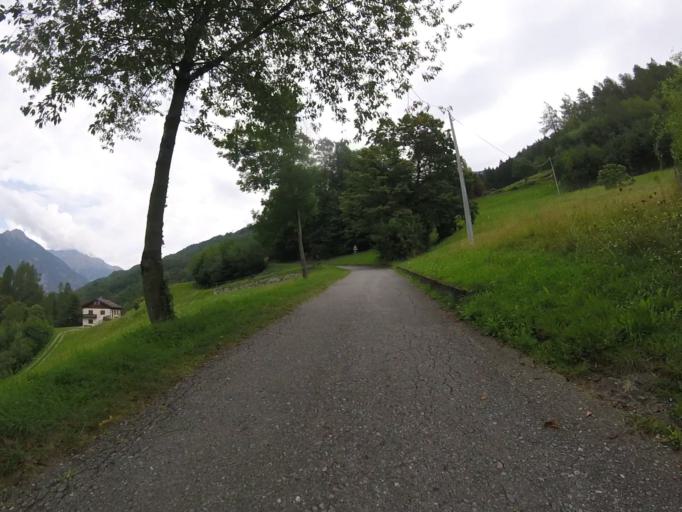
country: IT
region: Lombardy
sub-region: Provincia di Sondrio
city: Mazzo di Valtellina
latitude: 46.2634
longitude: 10.2700
